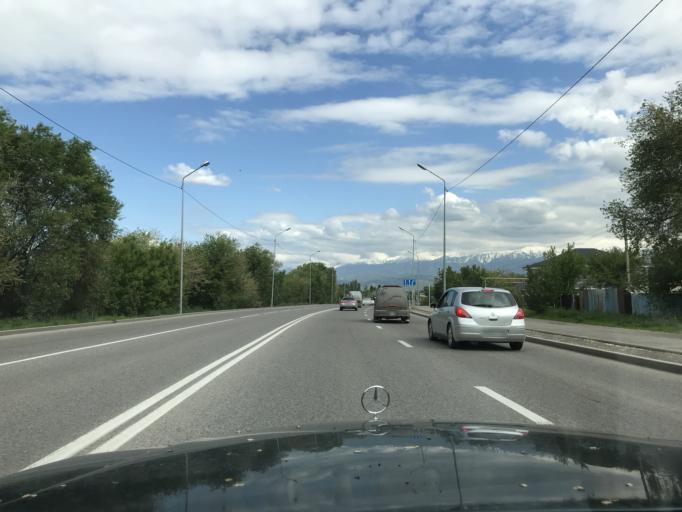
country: KZ
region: Almaty Oblysy
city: Burunday
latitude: 43.3117
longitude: 76.8645
